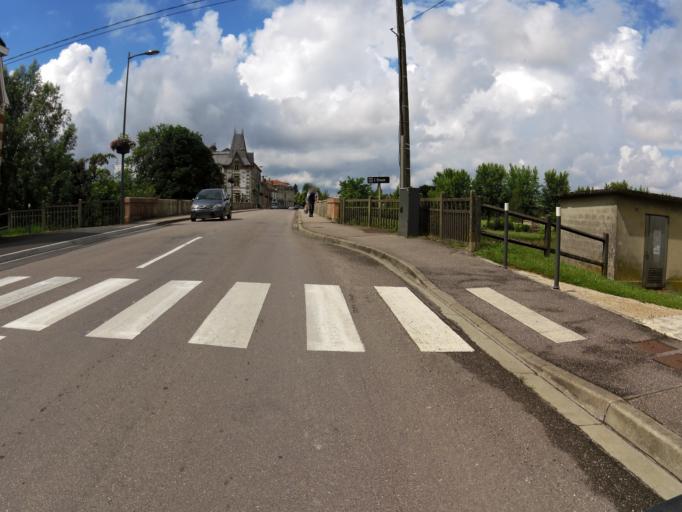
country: FR
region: Lorraine
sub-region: Departement de la Meuse
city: Revigny-sur-Ornain
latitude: 48.8250
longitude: 4.9856
